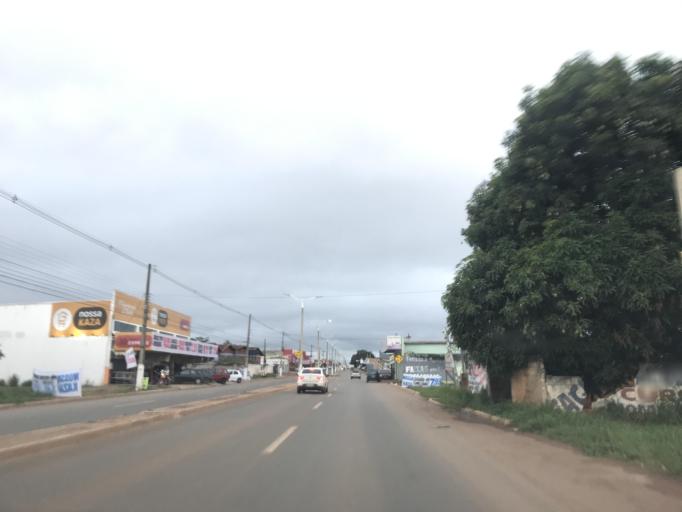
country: BR
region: Goias
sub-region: Luziania
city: Luziania
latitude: -16.2122
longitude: -47.9292
